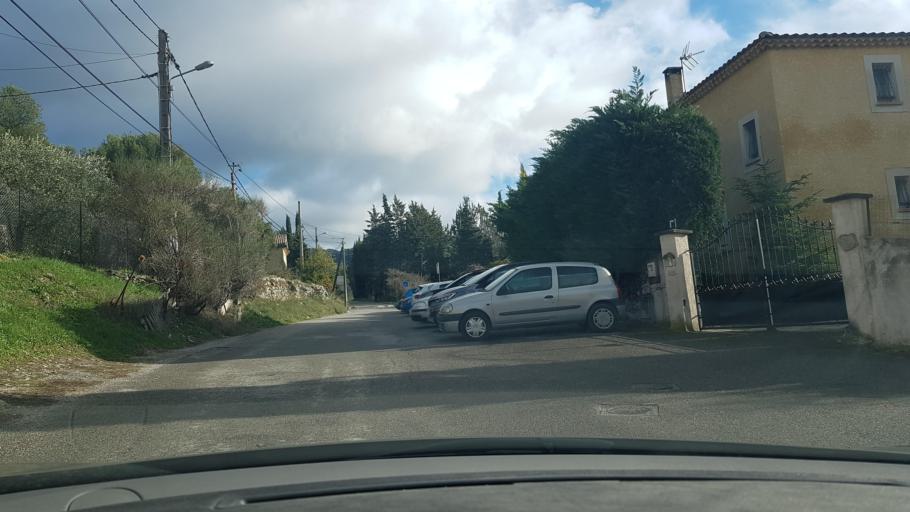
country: FR
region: Provence-Alpes-Cote d'Azur
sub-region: Departement des Bouches-du-Rhone
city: Simiane-Collongue
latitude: 43.4195
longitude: 5.4598
